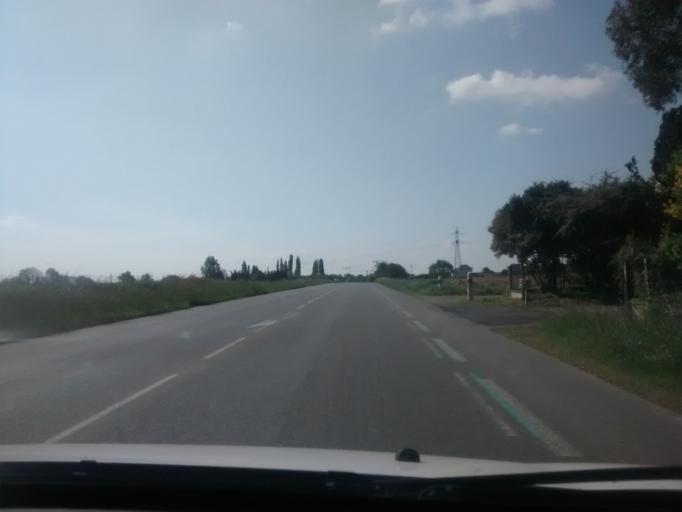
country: FR
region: Brittany
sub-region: Departement d'Ille-et-Vilaine
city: Montgermont
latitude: 48.1470
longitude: -1.7034
